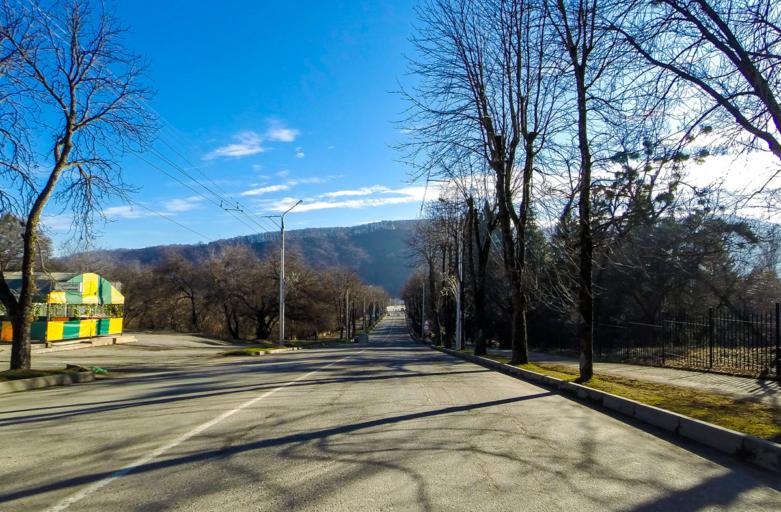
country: RU
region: Kabardino-Balkariya
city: Vol'nyy Aul
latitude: 43.4527
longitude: 43.5843
